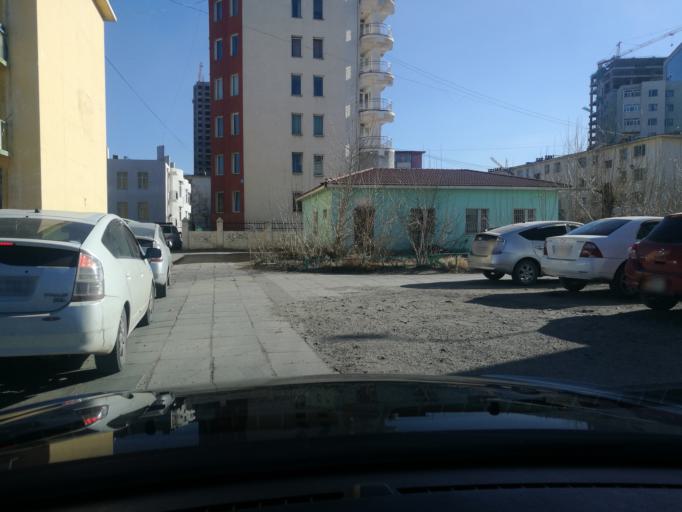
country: MN
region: Ulaanbaatar
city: Ulaanbaatar
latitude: 47.9022
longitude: 106.9075
